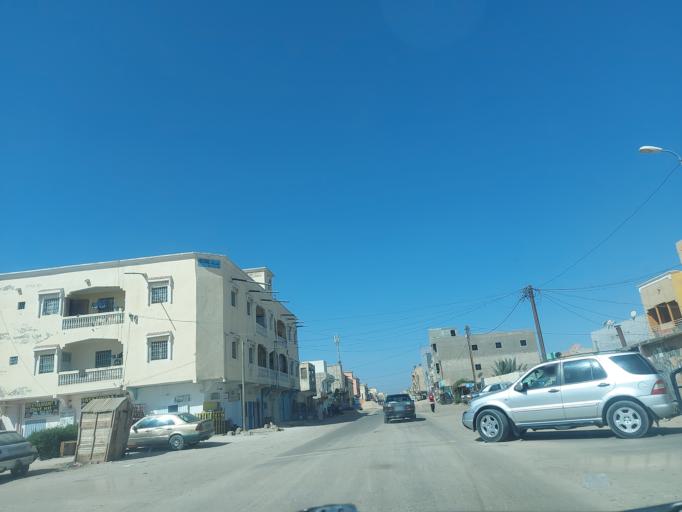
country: MR
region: Nouakchott
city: Nouakchott
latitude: 18.0797
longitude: -15.9907
